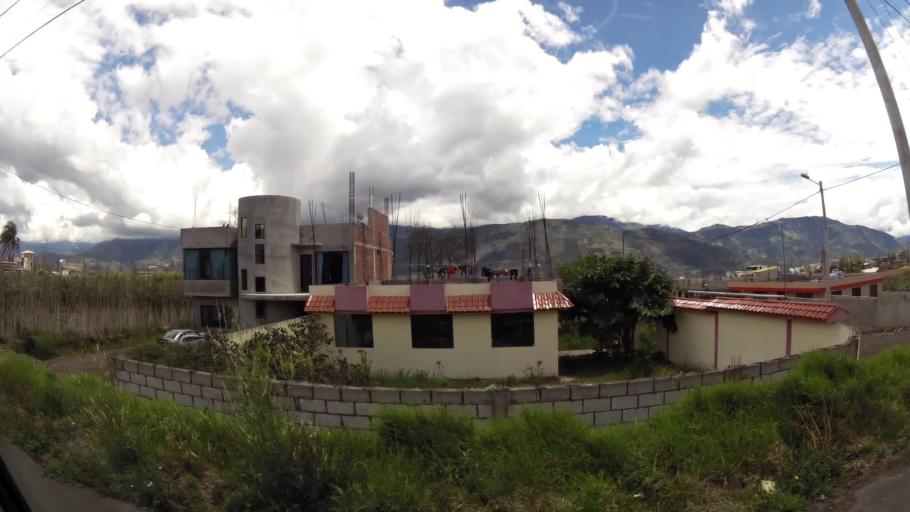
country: EC
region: Tungurahua
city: Pelileo
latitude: -1.3308
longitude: -78.5264
